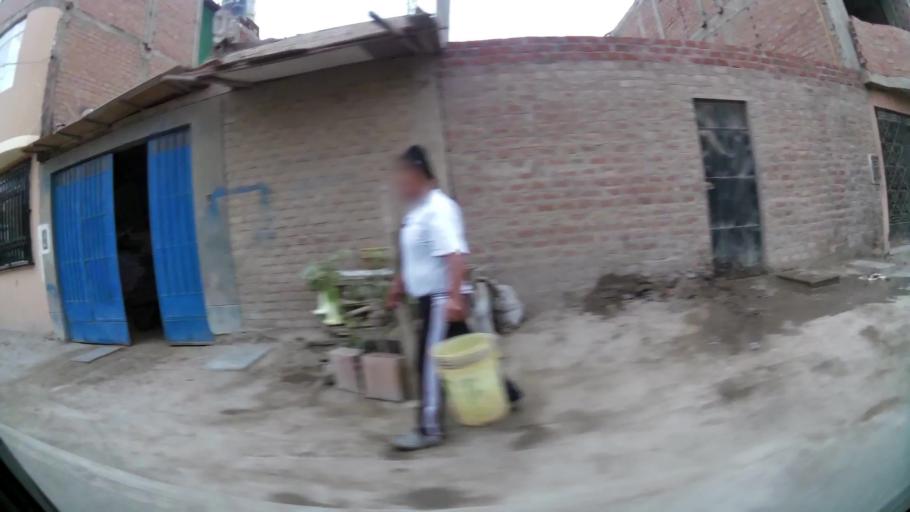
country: PE
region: Lima
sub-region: Lima
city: Independencia
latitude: -11.9767
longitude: -77.0979
